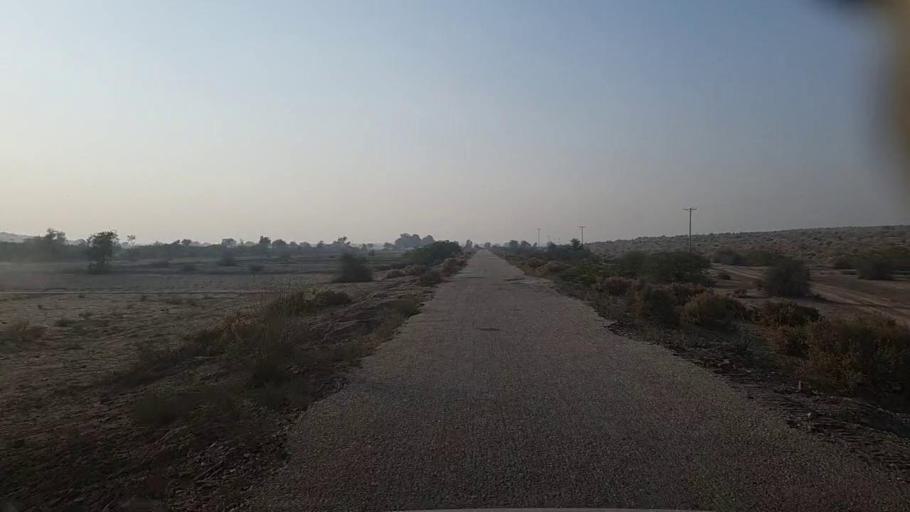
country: PK
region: Sindh
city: Pad Idan
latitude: 26.7142
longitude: 68.4691
